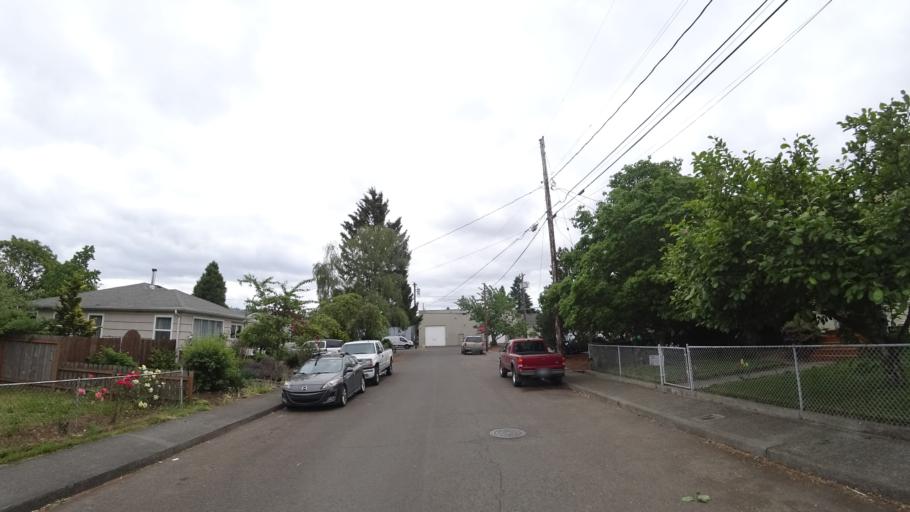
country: US
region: Oregon
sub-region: Multnomah County
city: Lents
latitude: 45.4827
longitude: -122.5759
